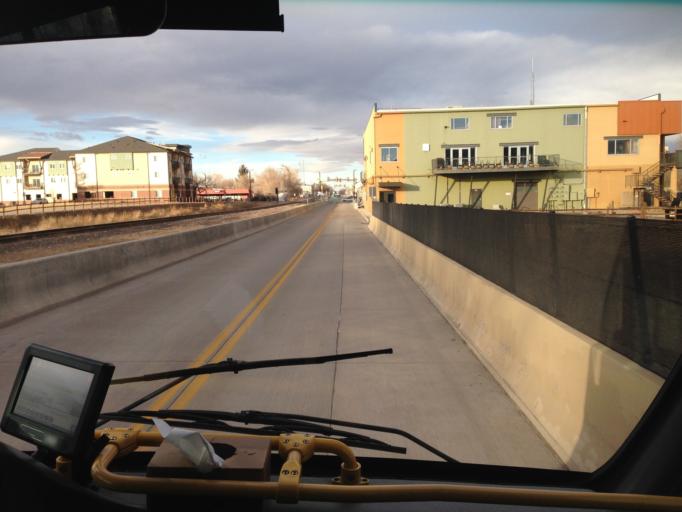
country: US
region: Colorado
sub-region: Larimer County
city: Fort Collins
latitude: 40.5653
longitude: -105.0788
